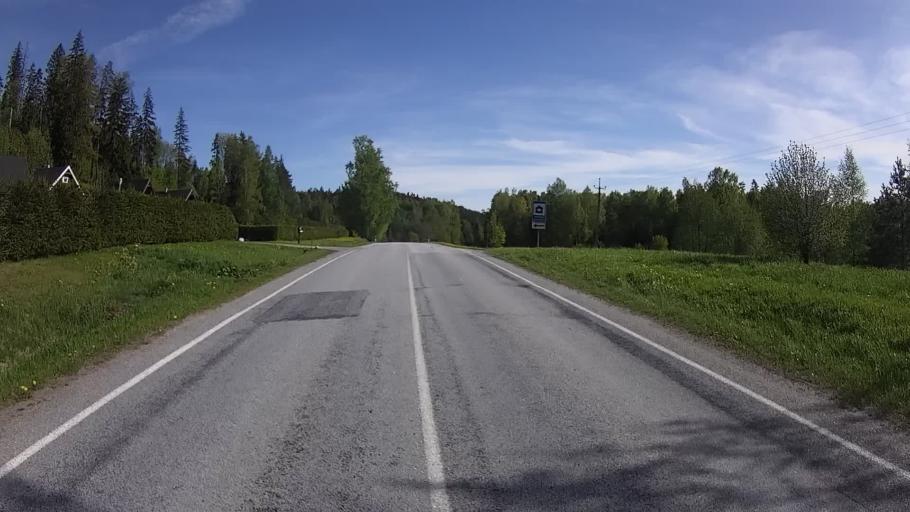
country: EE
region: Vorumaa
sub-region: Antsla vald
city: Vana-Antsla
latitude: 58.0372
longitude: 26.5078
